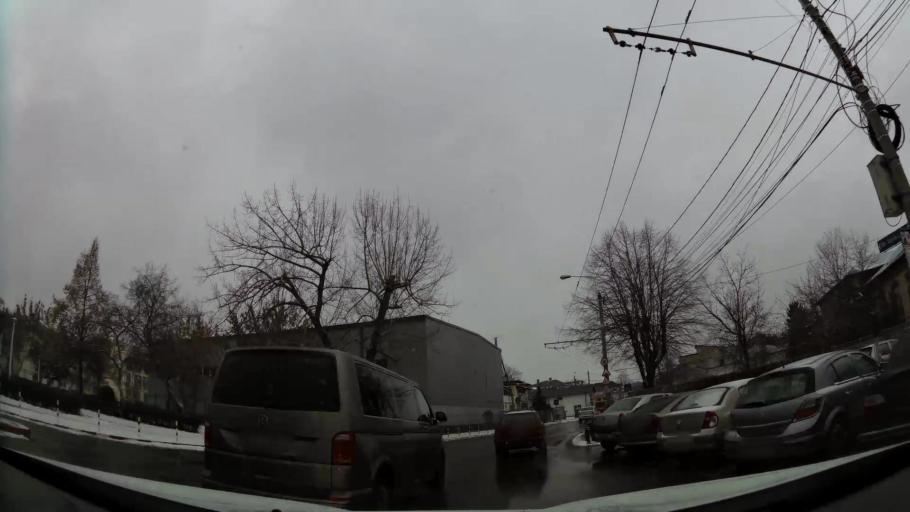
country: RO
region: Prahova
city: Ploiesti
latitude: 44.9420
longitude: 26.0172
